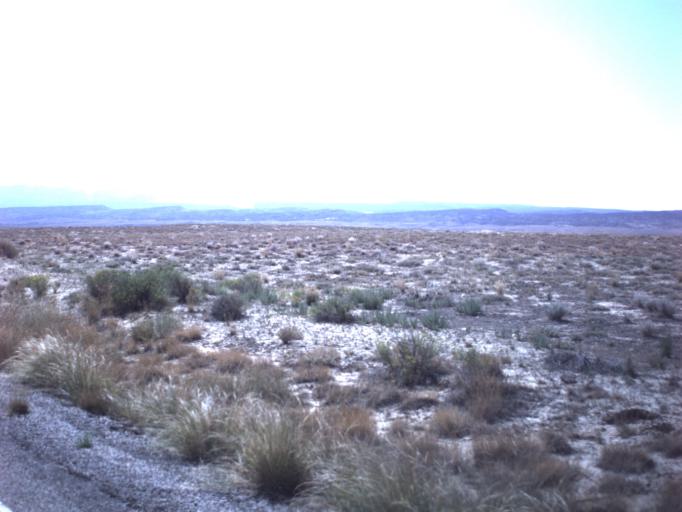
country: US
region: Utah
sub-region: Grand County
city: Moab
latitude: 38.9232
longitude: -109.3368
